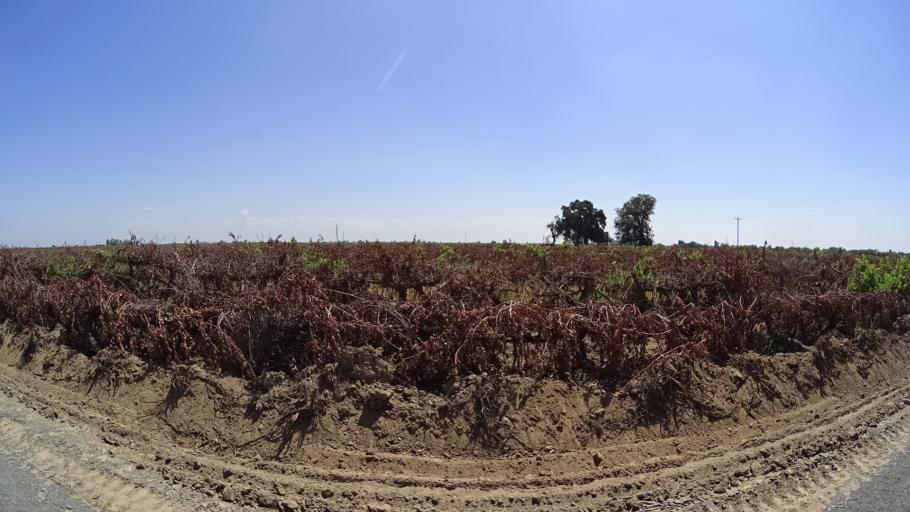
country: US
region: California
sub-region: Fresno County
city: Kingsburg
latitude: 36.4639
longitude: -119.6002
